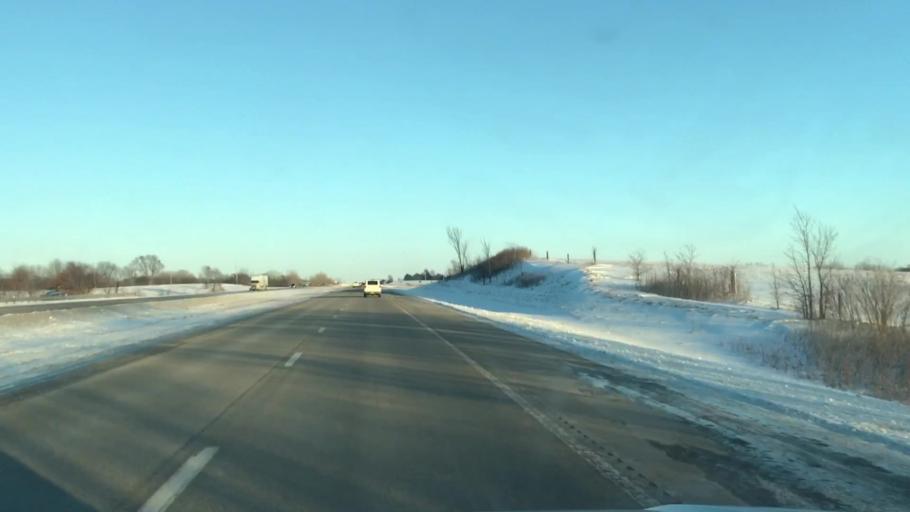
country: US
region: Missouri
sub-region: Clinton County
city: Gower
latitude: 39.7470
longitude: -94.6254
